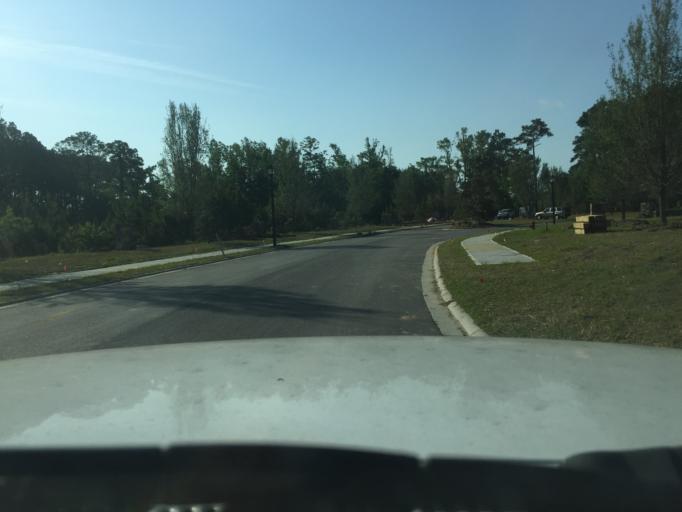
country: US
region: Georgia
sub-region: Chatham County
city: Georgetown
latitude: 32.0370
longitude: -81.2208
